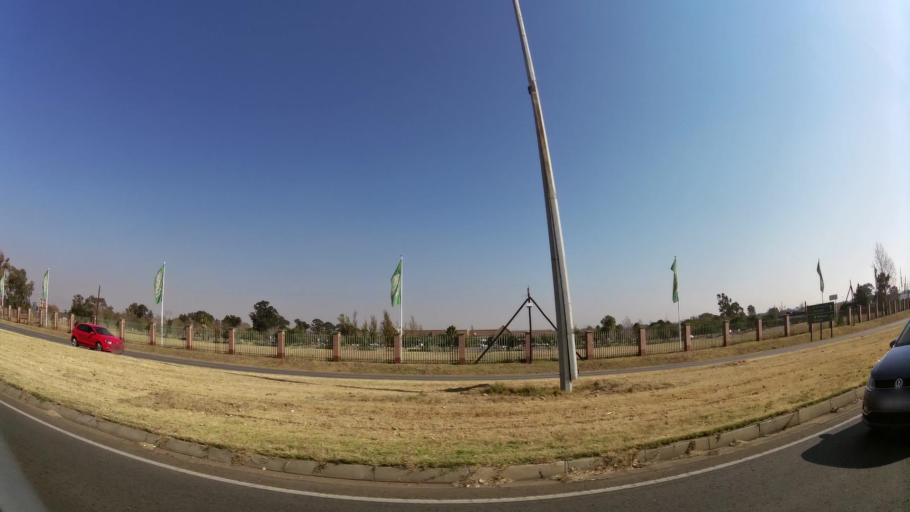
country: ZA
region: Gauteng
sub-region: Ekurhuleni Metropolitan Municipality
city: Boksburg
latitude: -26.2273
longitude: 28.2494
